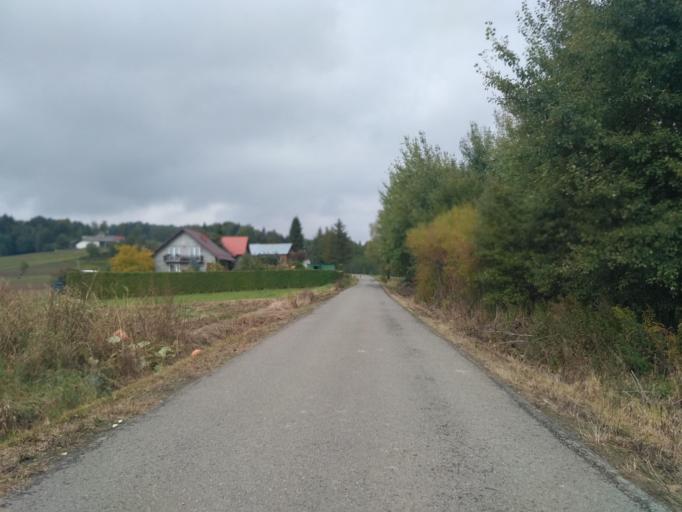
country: PL
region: Subcarpathian Voivodeship
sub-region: Powiat debicki
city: Brzostek
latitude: 49.9425
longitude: 21.4507
